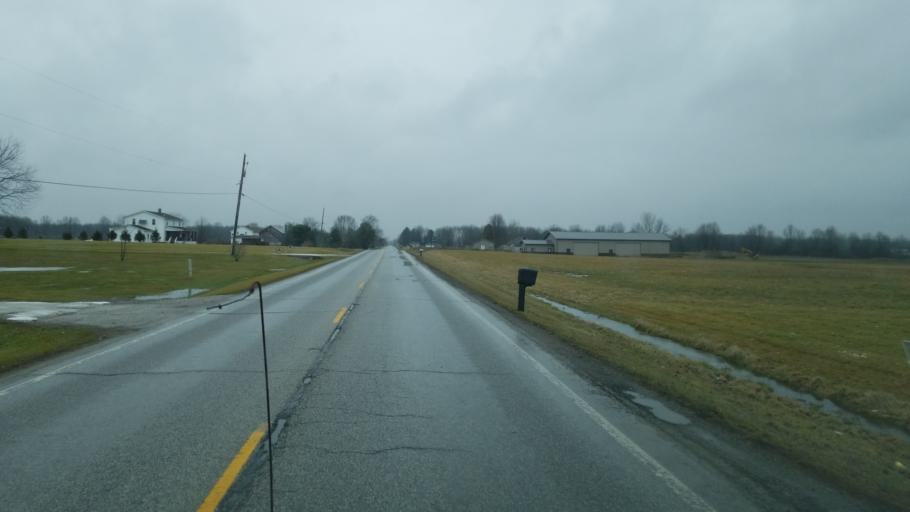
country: US
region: Ohio
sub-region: Geauga County
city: Middlefield
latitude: 41.4062
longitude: -80.9550
